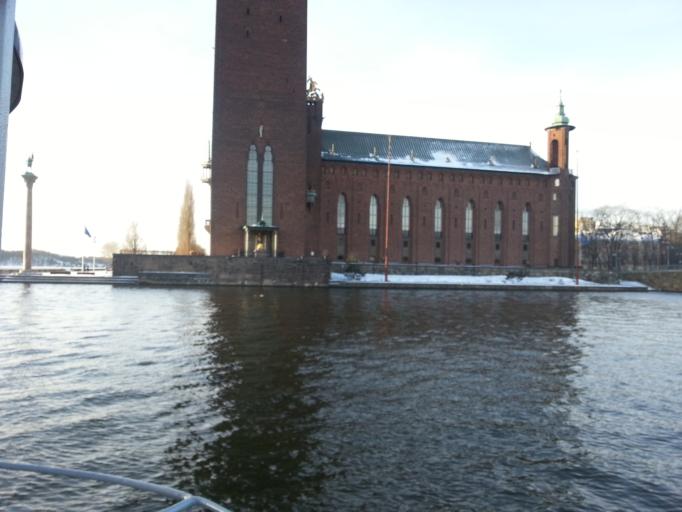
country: SE
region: Stockholm
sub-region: Stockholms Kommun
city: Stockholm
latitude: 59.3273
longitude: 18.0579
